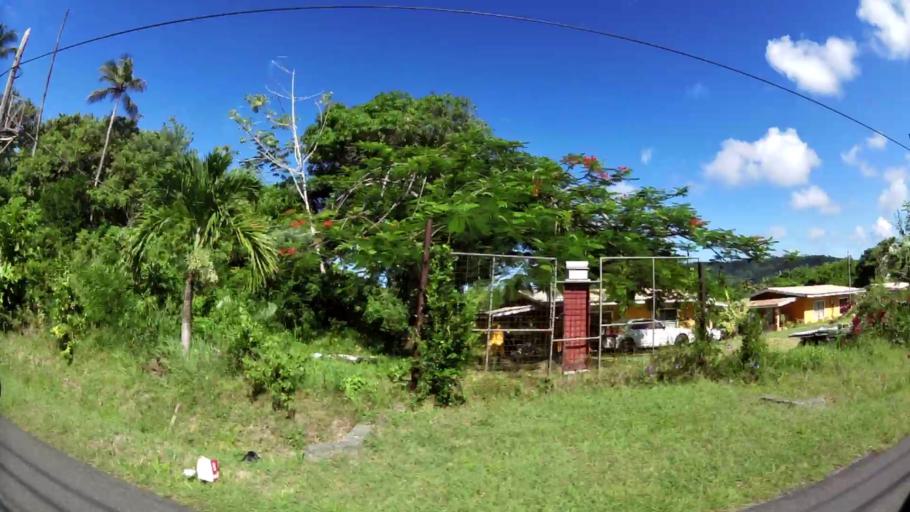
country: TT
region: Tobago
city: Scarborough
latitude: 11.1758
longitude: -60.7176
